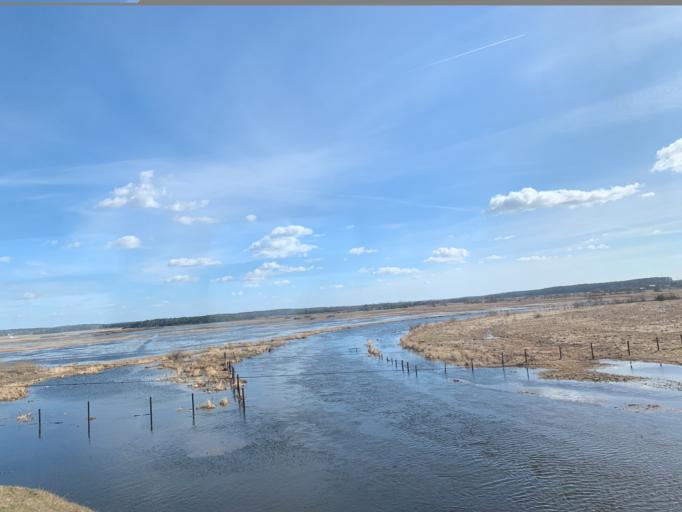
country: BY
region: Minsk
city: Novy Svyerzhan'
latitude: 53.4682
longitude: 26.7319
